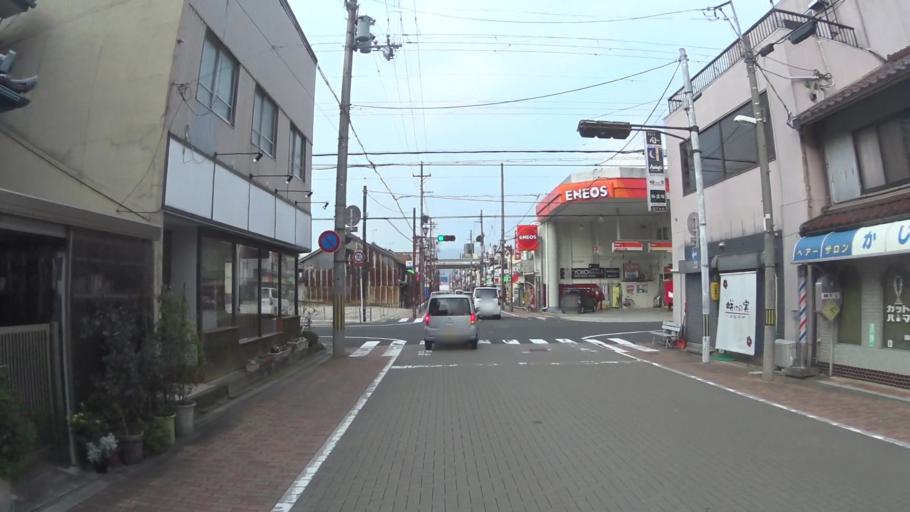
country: JP
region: Kyoto
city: Maizuru
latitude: 35.4729
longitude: 135.3961
